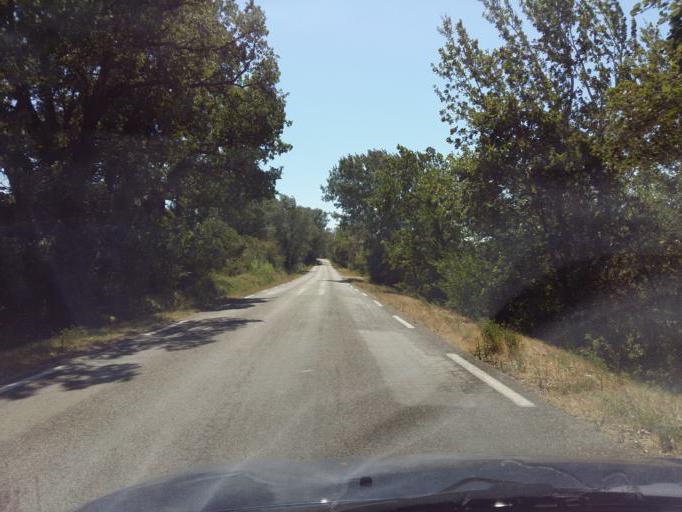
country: FR
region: Provence-Alpes-Cote d'Azur
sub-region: Departement du Vaucluse
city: Loriol-du-Comtat
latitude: 44.0955
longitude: 4.9928
